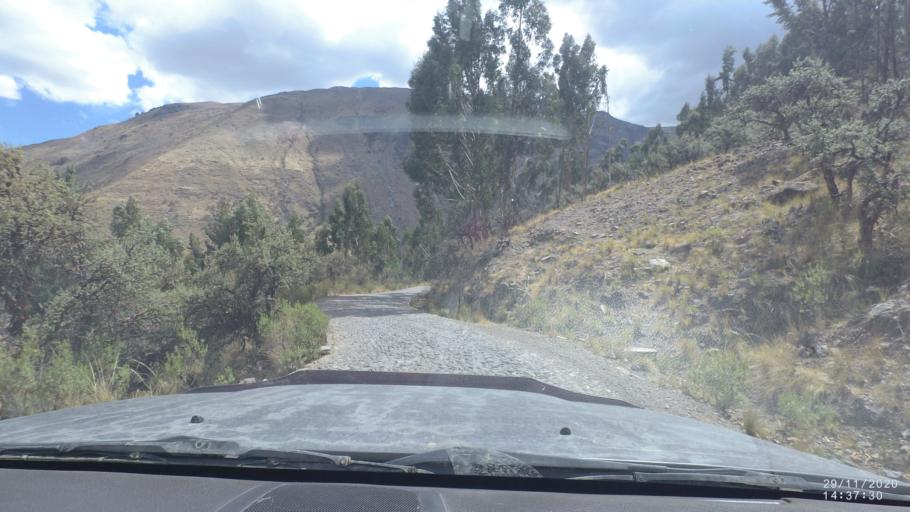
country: BO
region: Cochabamba
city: Sipe Sipe
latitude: -17.2713
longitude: -66.3288
